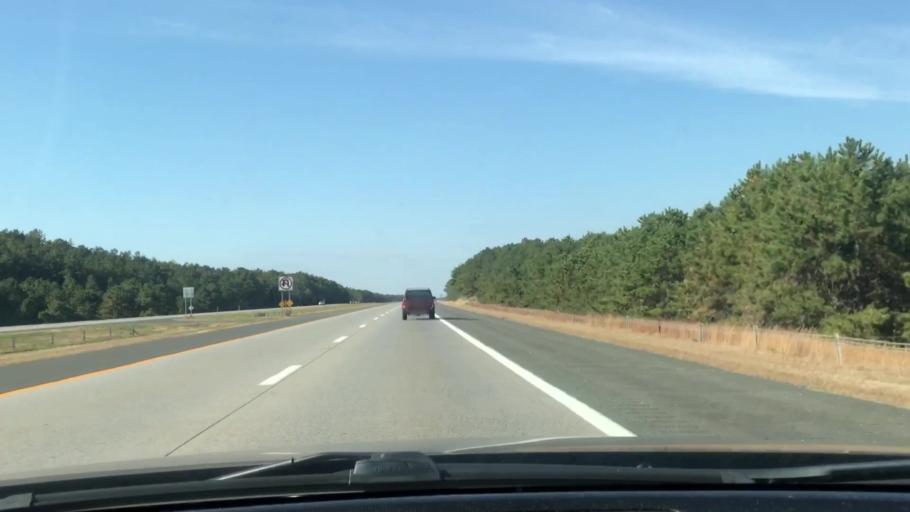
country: US
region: New York
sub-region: Suffolk County
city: East Quogue
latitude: 40.8755
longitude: -72.5707
